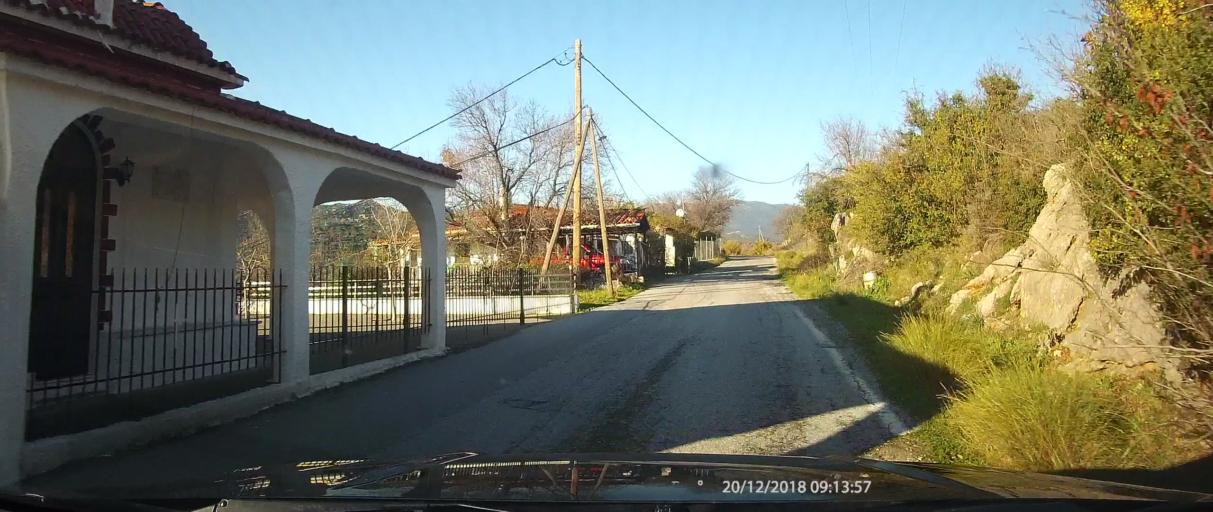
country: GR
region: Peloponnese
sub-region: Nomos Lakonias
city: Sykea
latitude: 36.8999
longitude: 22.9914
